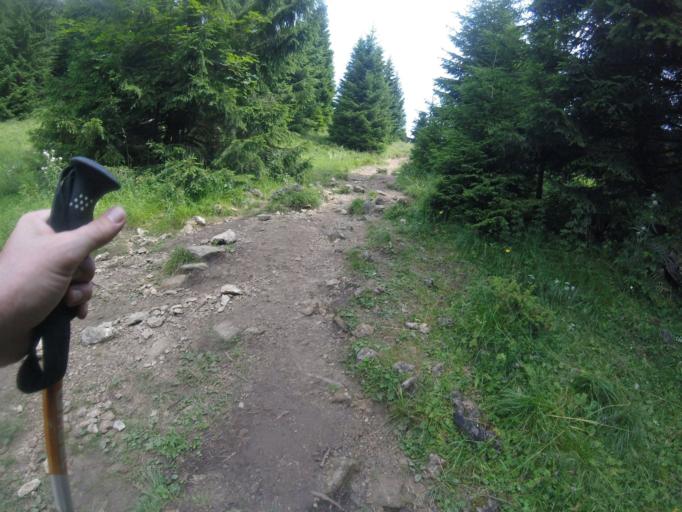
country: SK
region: Zilinsky
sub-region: Okres Zilina
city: Terchova
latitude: 49.2412
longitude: 19.0992
